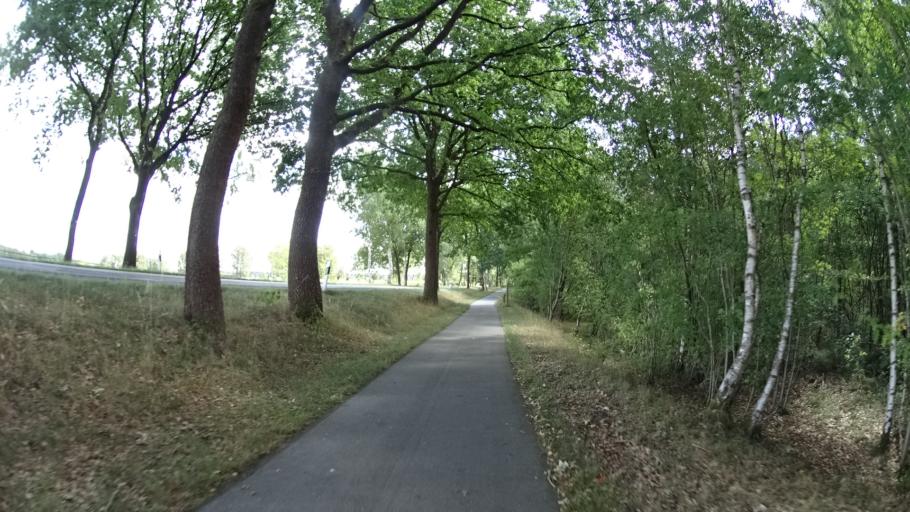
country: DE
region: Lower Saxony
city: Undeloh
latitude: 53.2218
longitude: 9.9351
